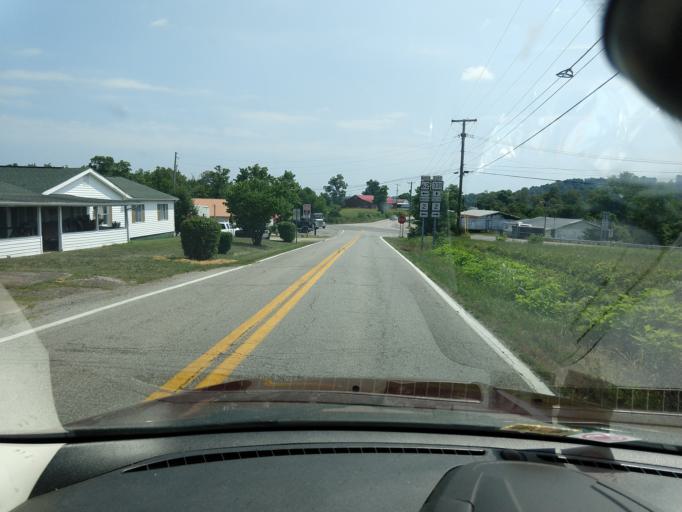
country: US
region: West Virginia
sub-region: Jackson County
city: Ravenswood
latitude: 38.8648
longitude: -81.8847
